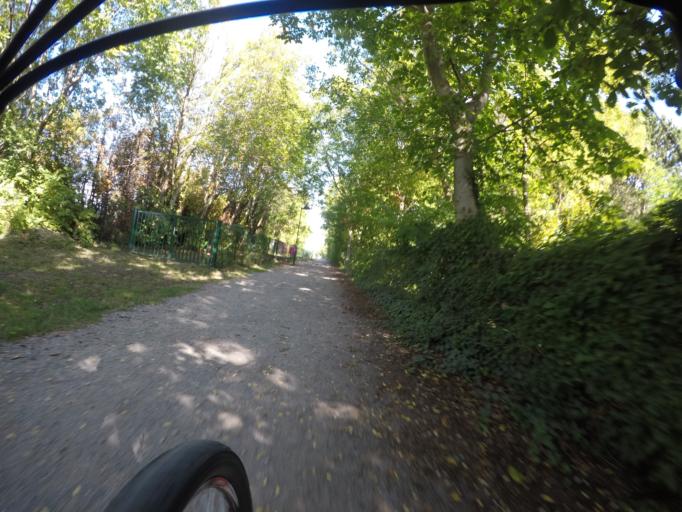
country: AT
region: Lower Austria
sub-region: Politischer Bezirk Modling
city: Brunn am Gebirge
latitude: 48.1043
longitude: 16.2990
